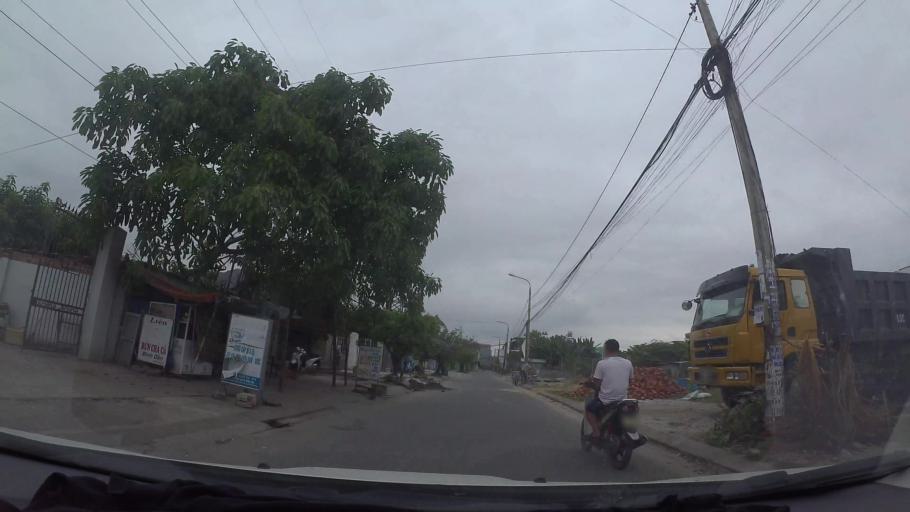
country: VN
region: Da Nang
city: Lien Chieu
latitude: 16.0694
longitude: 108.1445
